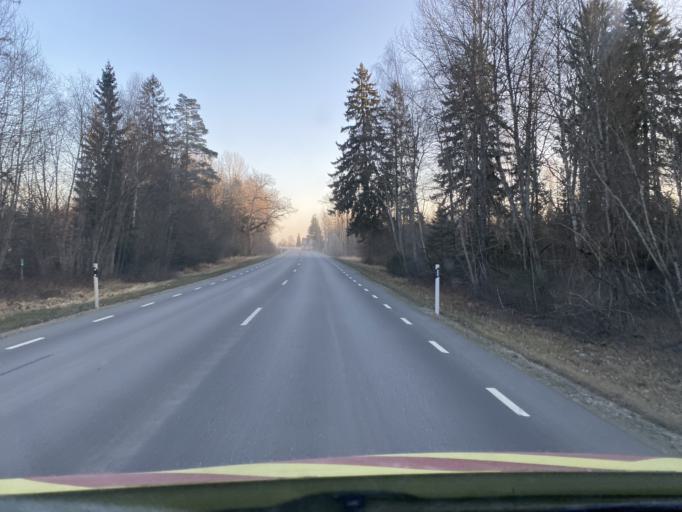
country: EE
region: Raplamaa
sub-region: Maerjamaa vald
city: Marjamaa
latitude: 58.9266
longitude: 24.3911
